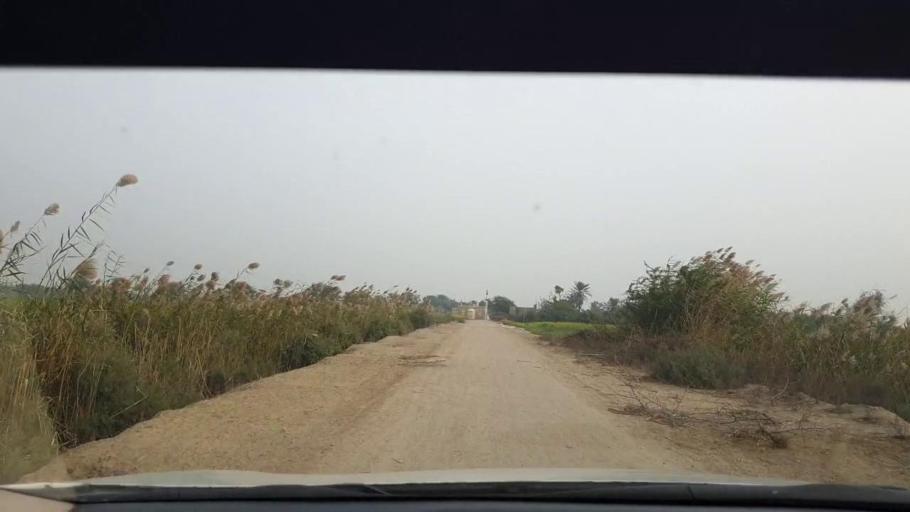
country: PK
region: Sindh
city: Berani
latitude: 25.8380
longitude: 68.8477
